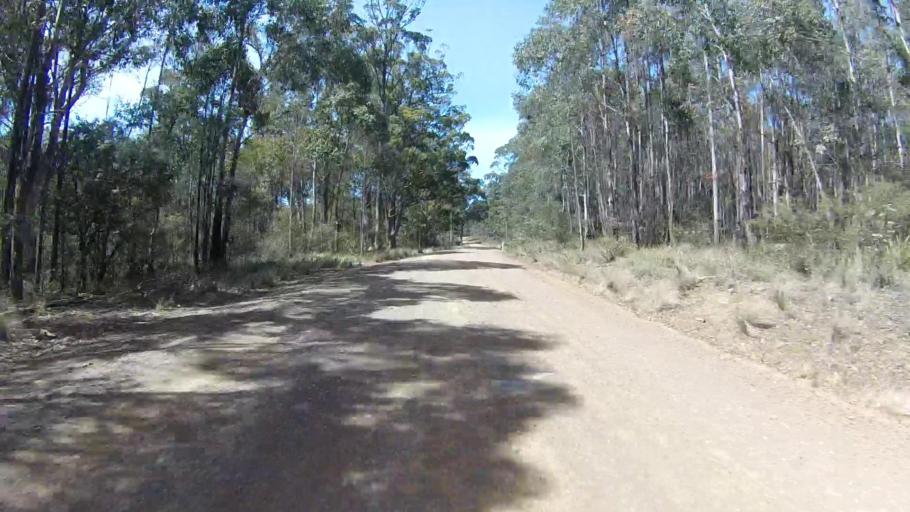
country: AU
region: Tasmania
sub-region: Sorell
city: Sorell
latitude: -42.6660
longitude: 147.7300
